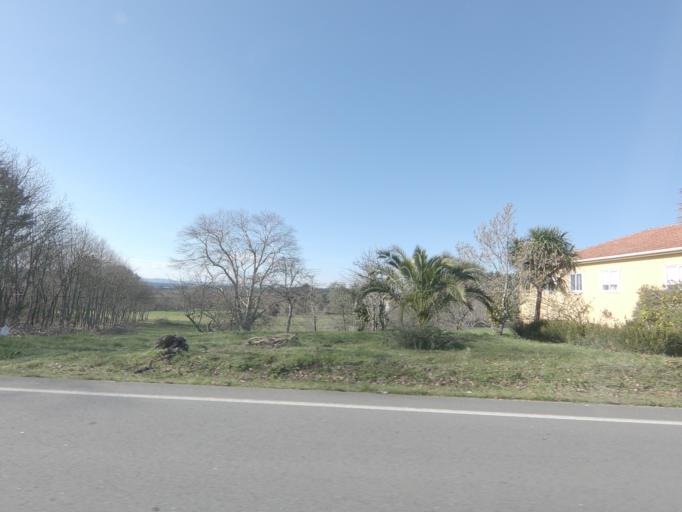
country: ES
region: Galicia
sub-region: Provincia da Coruna
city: Ribeira
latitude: 42.7175
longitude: -8.4432
